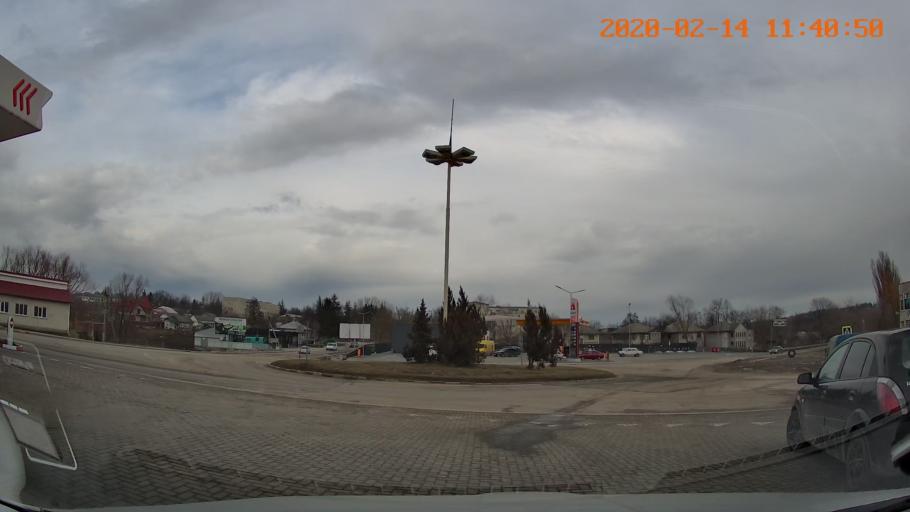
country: MD
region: Briceni
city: Briceni
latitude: 48.3503
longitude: 27.0840
